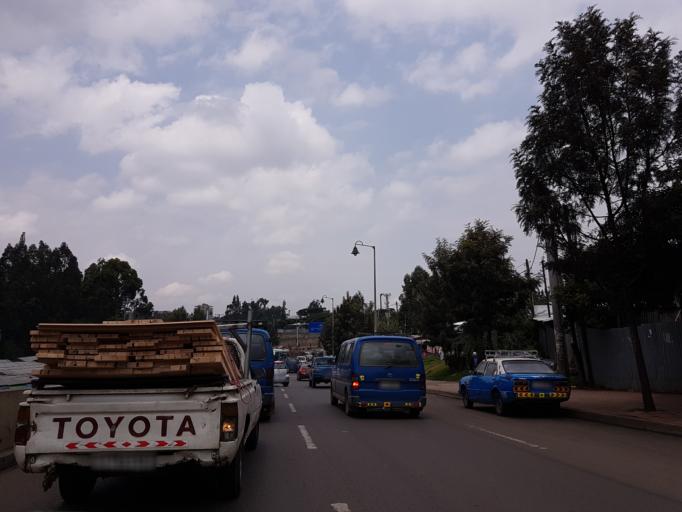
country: ET
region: Adis Abeba
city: Addis Ababa
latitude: 9.0052
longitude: 38.7338
